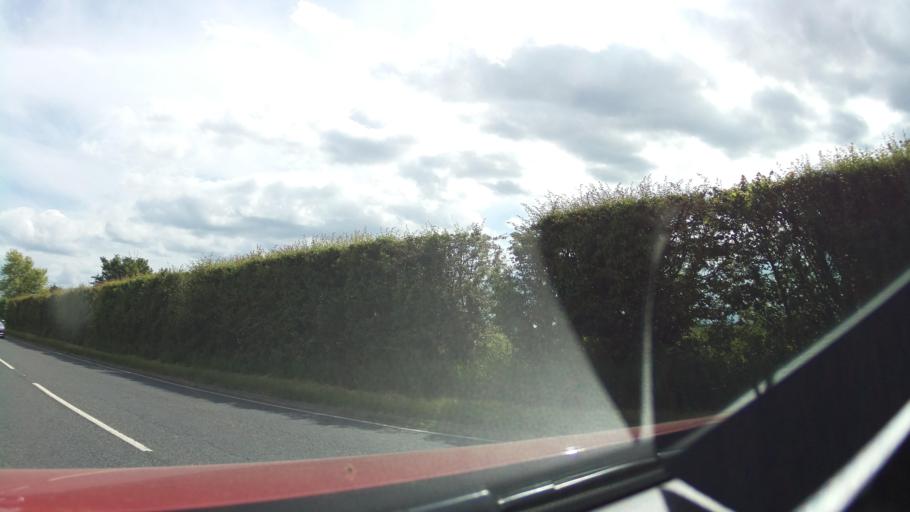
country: GB
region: England
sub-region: Worcestershire
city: Pershore
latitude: 52.1245
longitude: -2.1037
